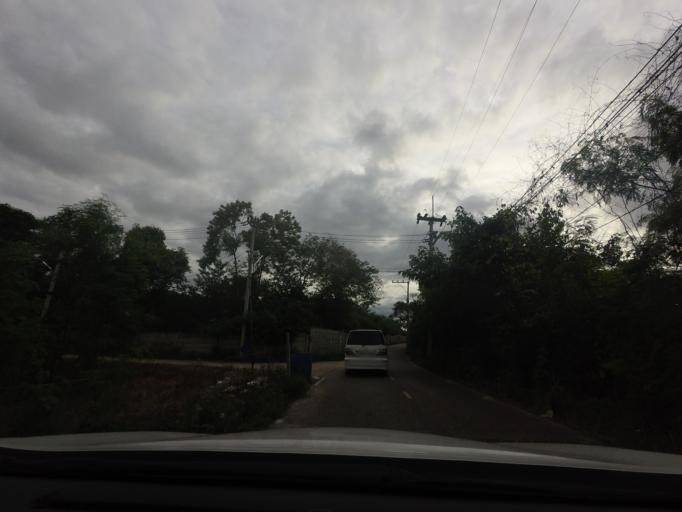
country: TH
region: Nakhon Ratchasima
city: Pak Chong
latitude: 14.6089
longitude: 101.4104
